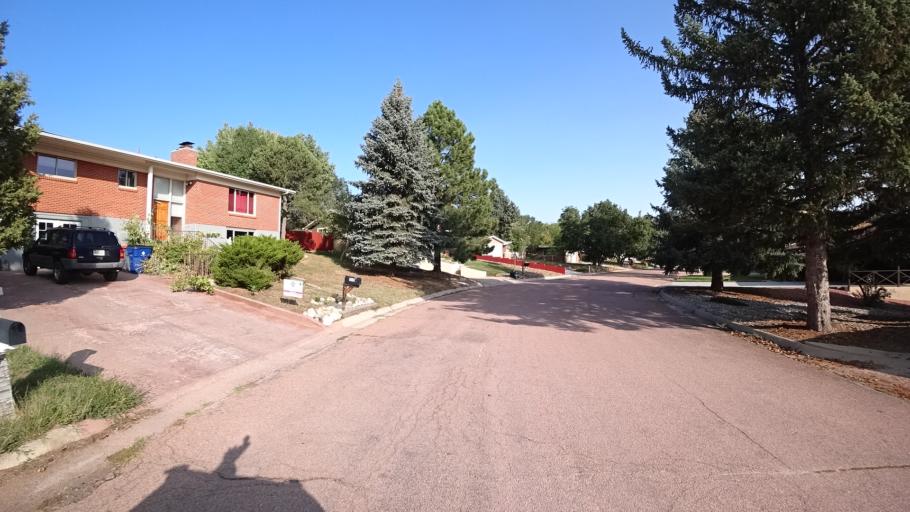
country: US
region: Colorado
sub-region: El Paso County
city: Colorado Springs
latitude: 38.8203
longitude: -104.8656
